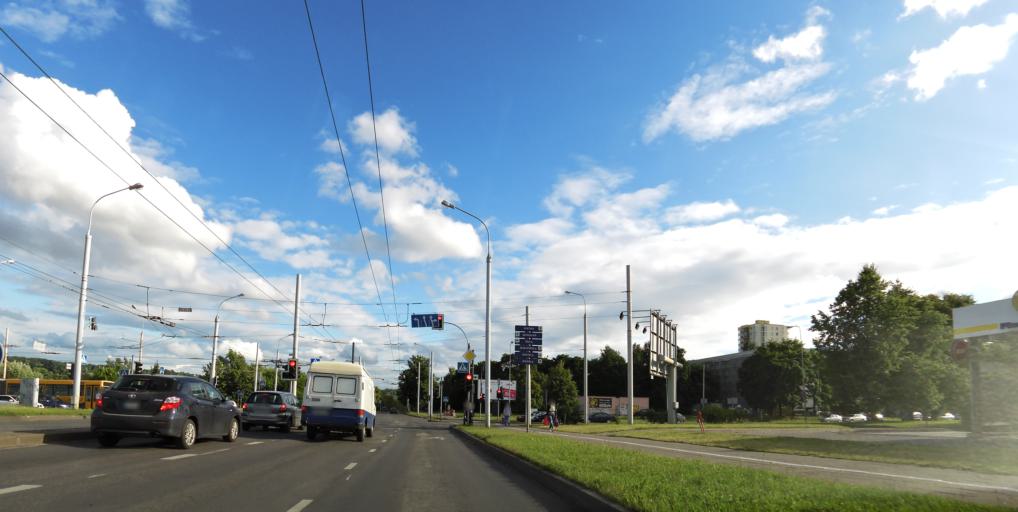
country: LT
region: Vilnius County
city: Rasos
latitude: 54.7062
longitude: 25.3044
